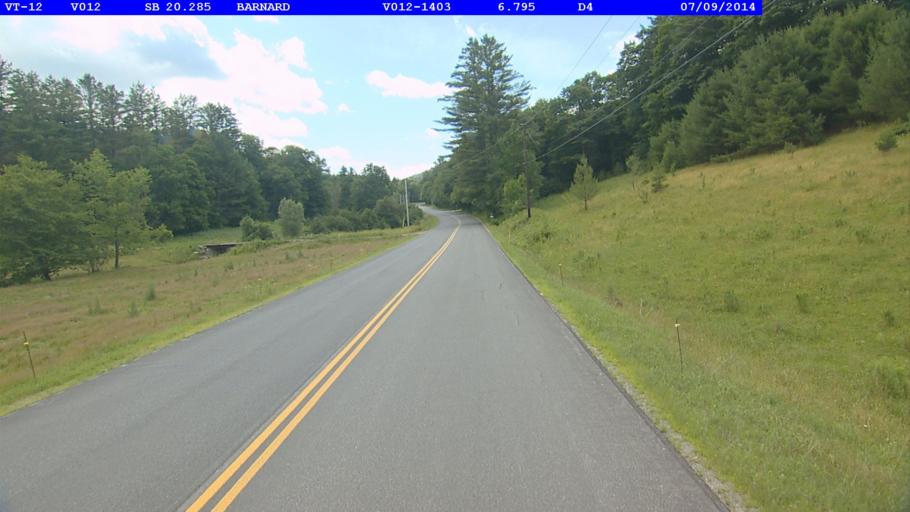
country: US
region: Vermont
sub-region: Orange County
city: Randolph
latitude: 43.7547
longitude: -72.6334
